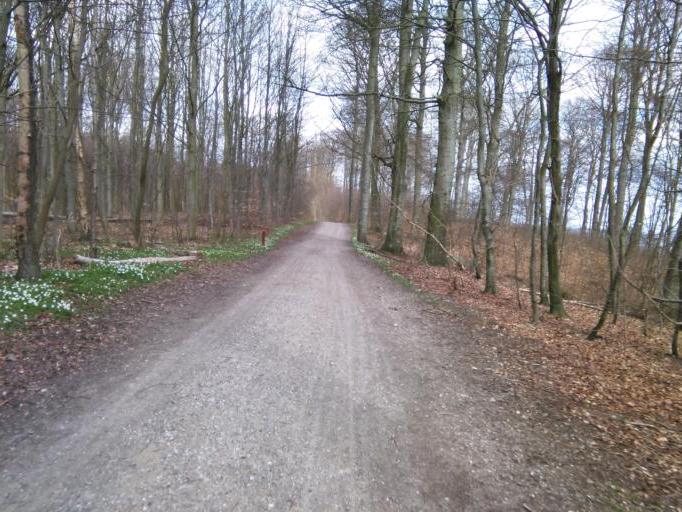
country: DK
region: Central Jutland
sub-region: Arhus Kommune
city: Beder
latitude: 56.0795
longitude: 10.2512
